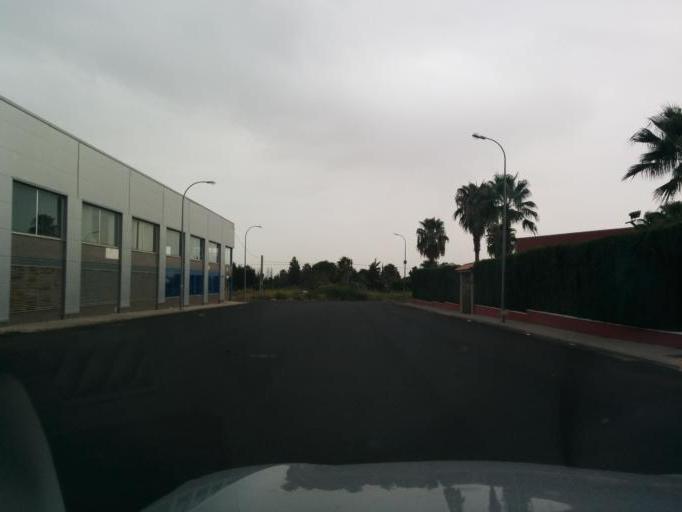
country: ES
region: Andalusia
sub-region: Provincia de Sevilla
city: Guillena
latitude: 37.5563
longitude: -6.0315
